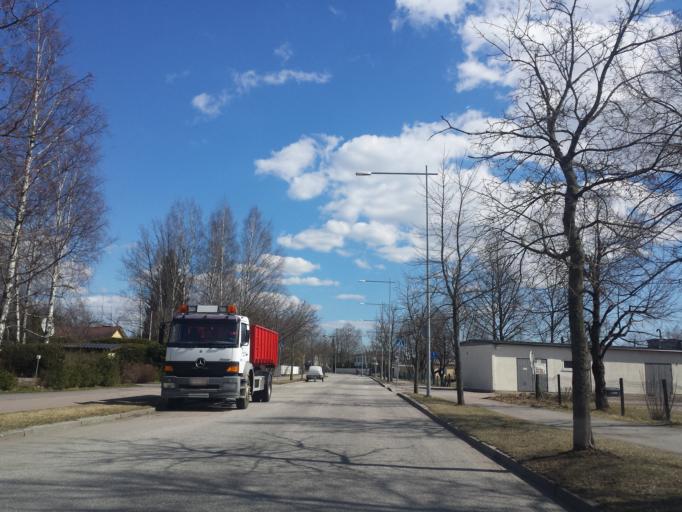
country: FI
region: Uusimaa
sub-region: Helsinki
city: Vantaa
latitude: 60.2980
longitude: 25.0205
